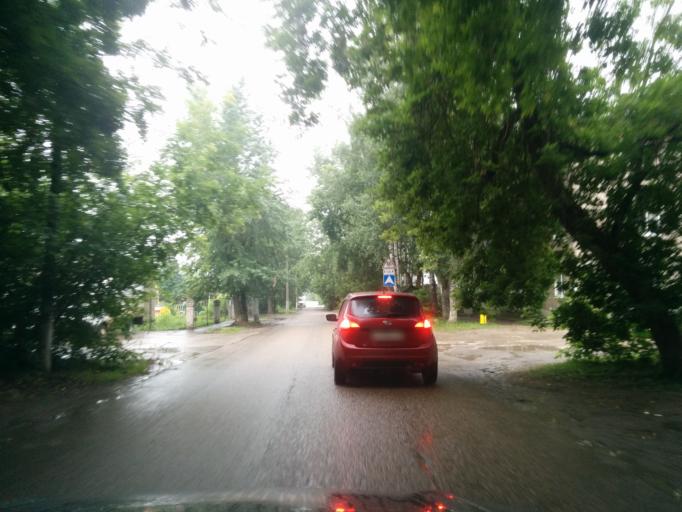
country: RU
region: Perm
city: Kondratovo
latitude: 58.0341
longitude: 56.0344
